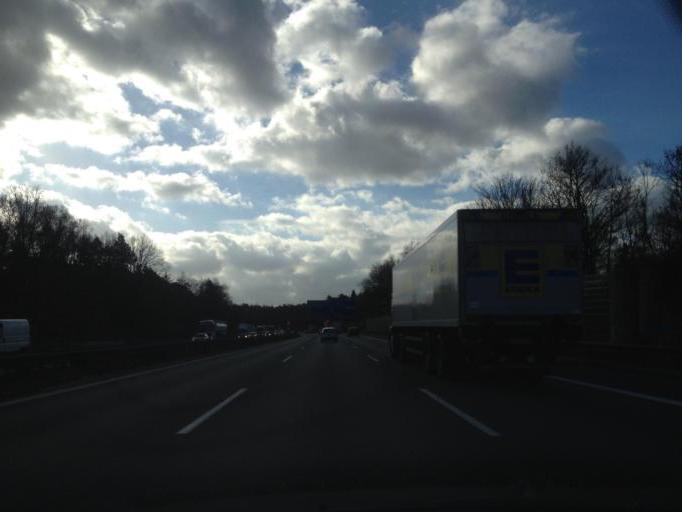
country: DE
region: Bavaria
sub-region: Regierungsbezirk Mittelfranken
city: Feucht
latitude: 49.4167
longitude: 11.2002
